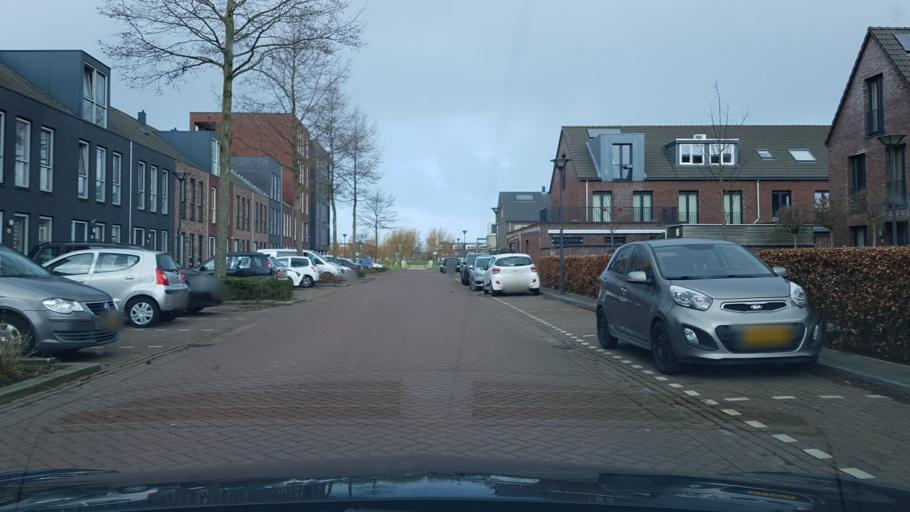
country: NL
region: North Holland
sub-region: Gemeente Bloemendaal
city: Bennebroek
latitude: 52.3035
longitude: 4.6338
